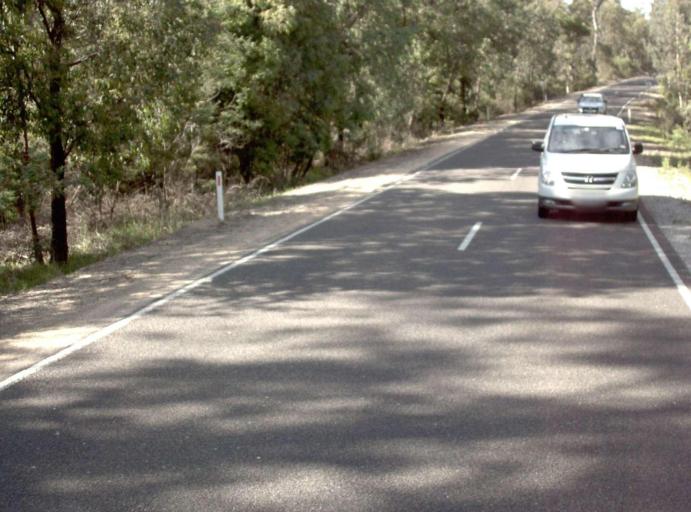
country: AU
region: Victoria
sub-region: East Gippsland
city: Lakes Entrance
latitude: -37.6084
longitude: 148.1189
